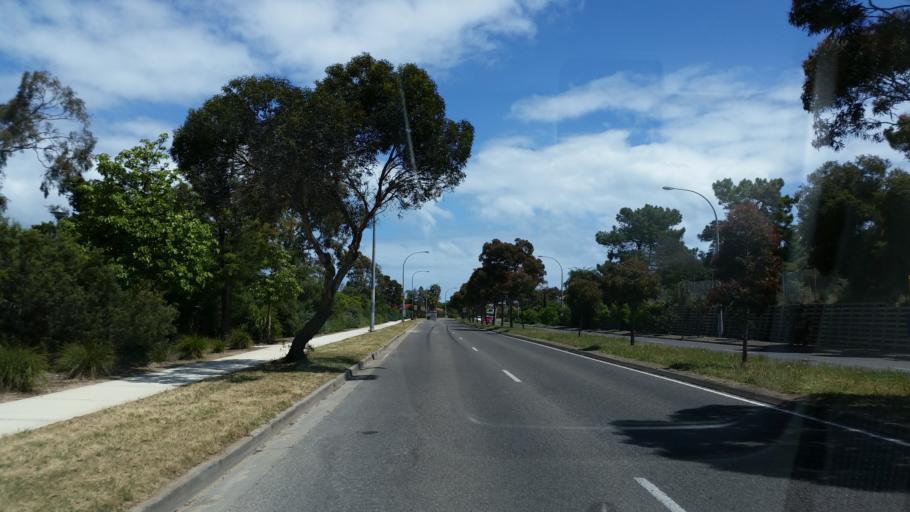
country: AU
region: South Australia
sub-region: Charles Sturt
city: Grange
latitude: -34.8928
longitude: 138.4964
